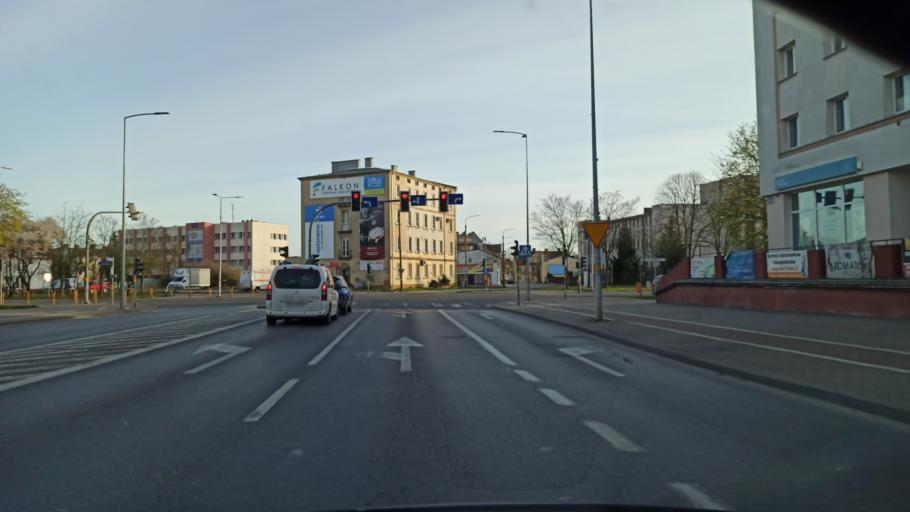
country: PL
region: Warmian-Masurian Voivodeship
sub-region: Powiat elblaski
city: Elblag
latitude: 54.1567
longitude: 19.4044
